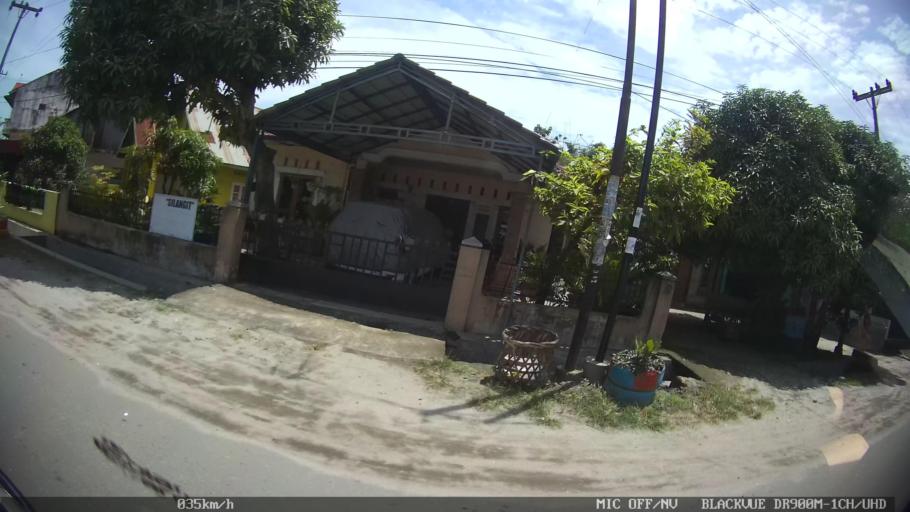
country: ID
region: North Sumatra
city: Perbaungan
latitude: 3.5462
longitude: 98.8796
